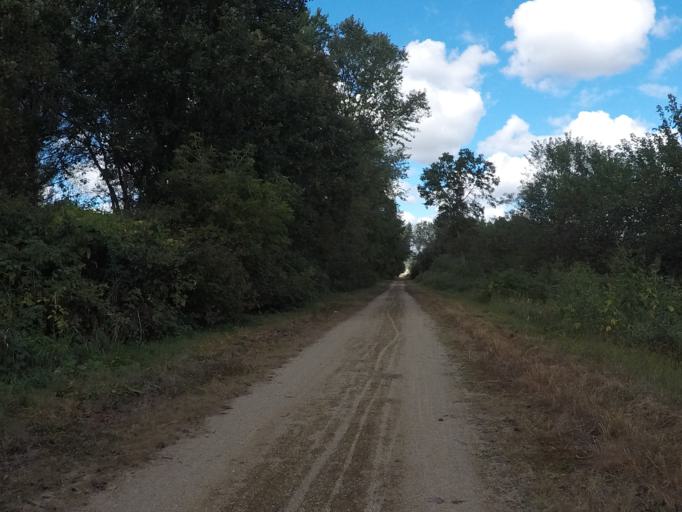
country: US
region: Wisconsin
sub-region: Richland County
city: Richland Center
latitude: 43.3062
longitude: -90.3417
